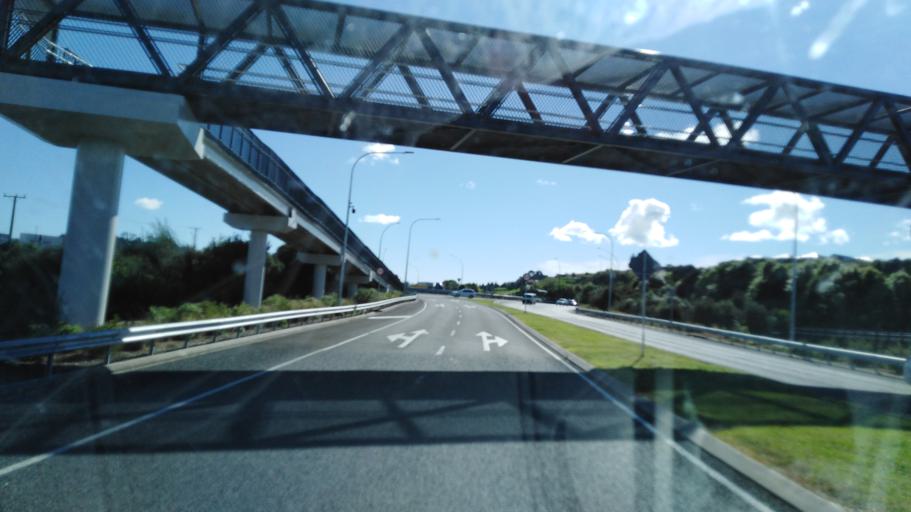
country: NZ
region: Bay of Plenty
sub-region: Tauranga City
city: Tauranga
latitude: -37.7398
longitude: 176.1071
